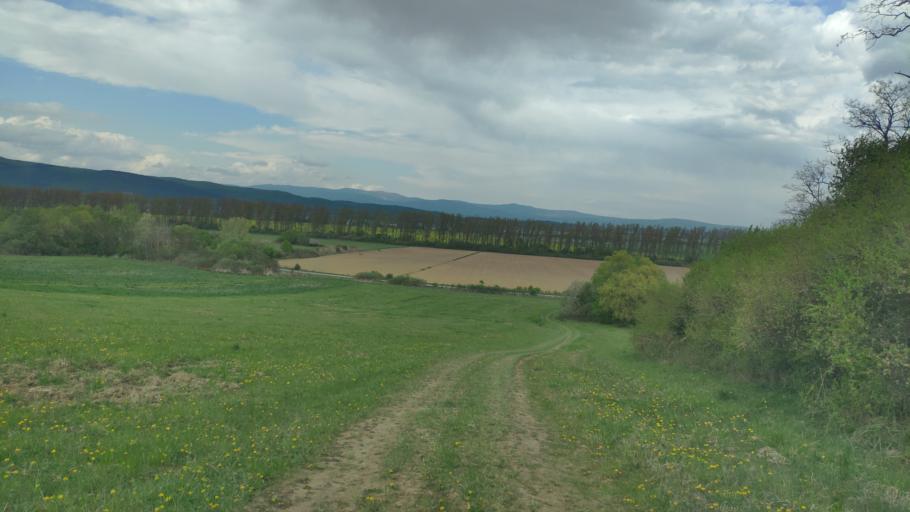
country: SK
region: Kosicky
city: Moldava nad Bodvou
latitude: 48.5580
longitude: 20.9549
